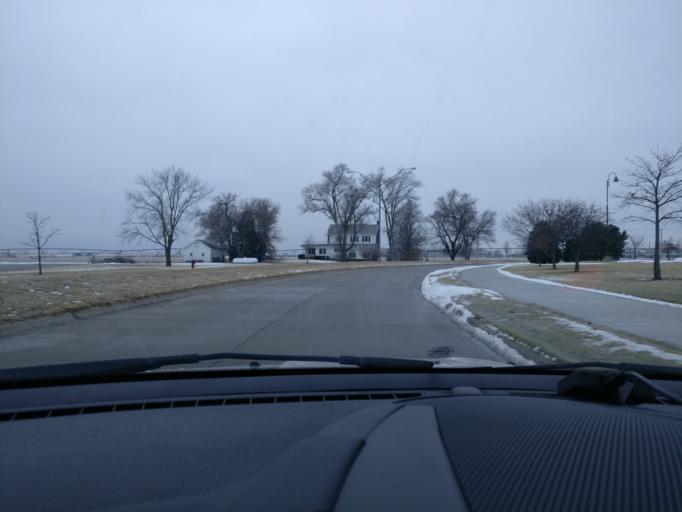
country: US
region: Nebraska
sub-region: Dodge County
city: Fremont
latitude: 41.4456
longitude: -96.4521
